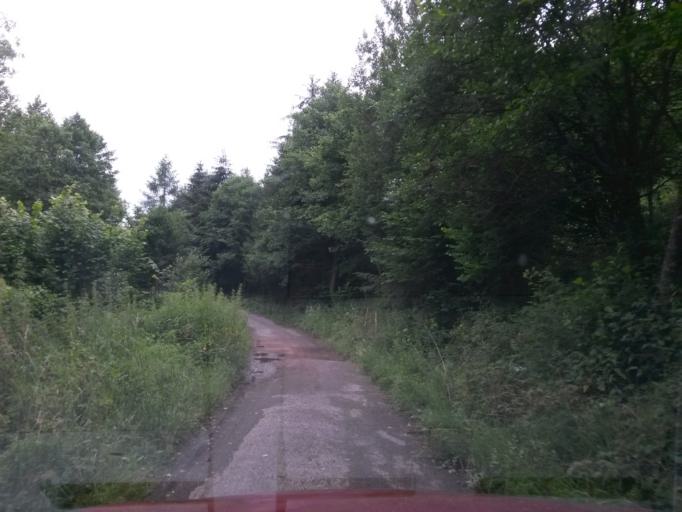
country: SK
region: Banskobystricky
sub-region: Okres Banska Bystrica
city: Zvolen
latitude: 48.5071
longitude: 19.2596
